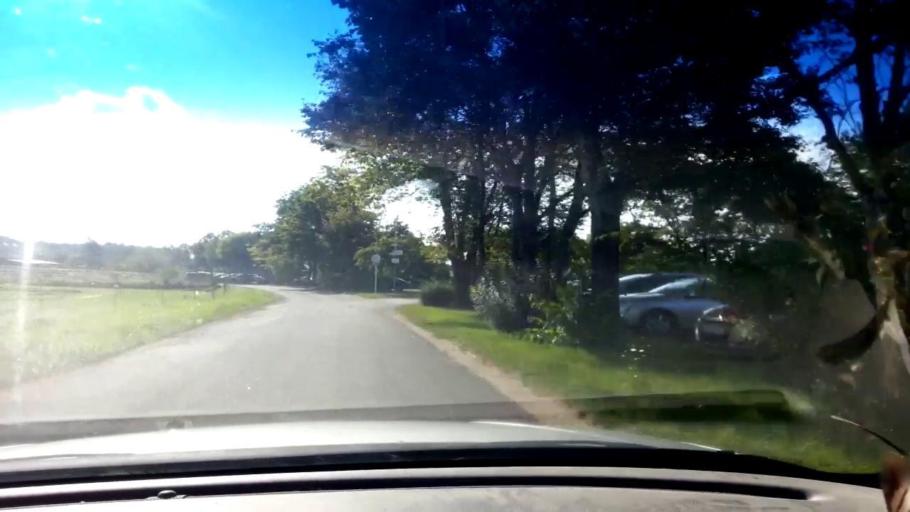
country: DE
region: Bavaria
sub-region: Upper Franconia
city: Bischberg
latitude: 49.8916
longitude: 10.8282
